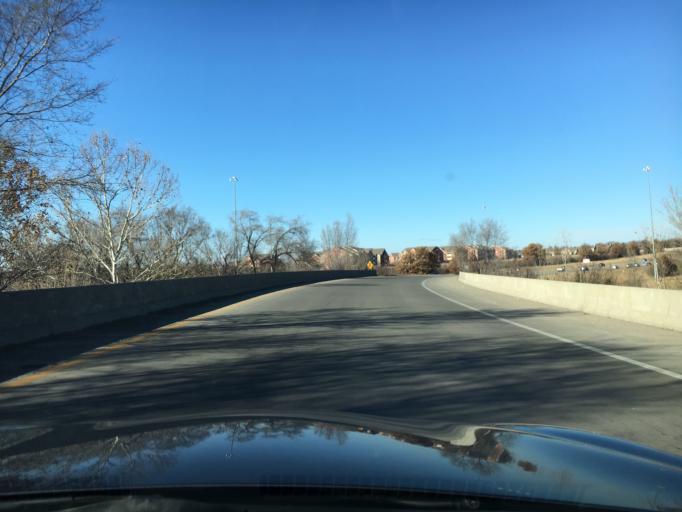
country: US
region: Kansas
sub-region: Johnson County
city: Lenexa
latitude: 38.8845
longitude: -94.6751
